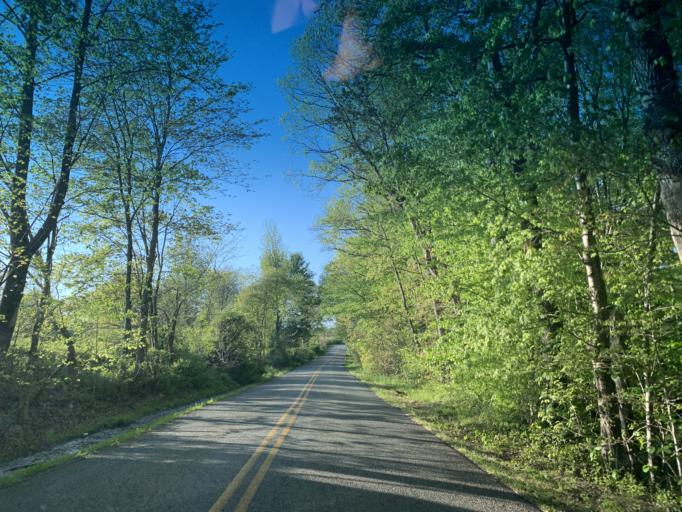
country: US
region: Maryland
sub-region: Harford County
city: Aberdeen
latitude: 39.5463
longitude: -76.1795
